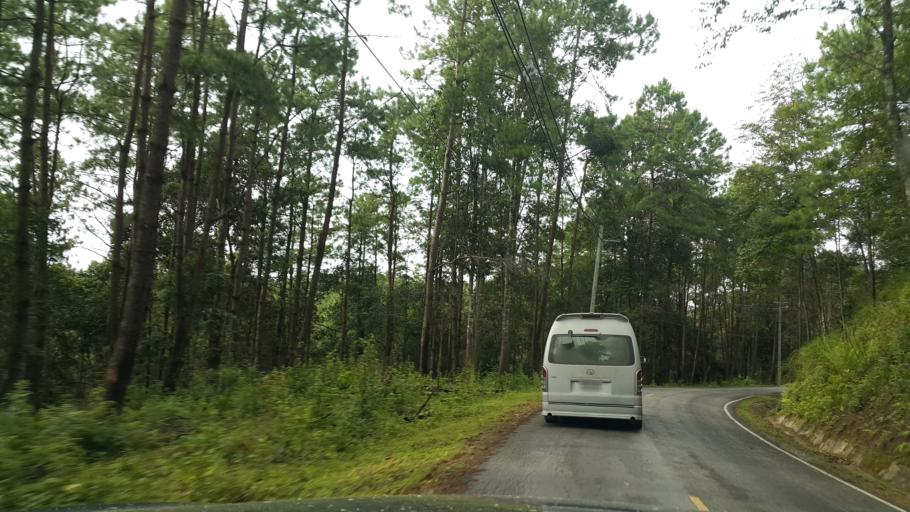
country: TH
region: Chiang Mai
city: Chaem Luang
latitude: 18.9249
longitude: 98.4773
